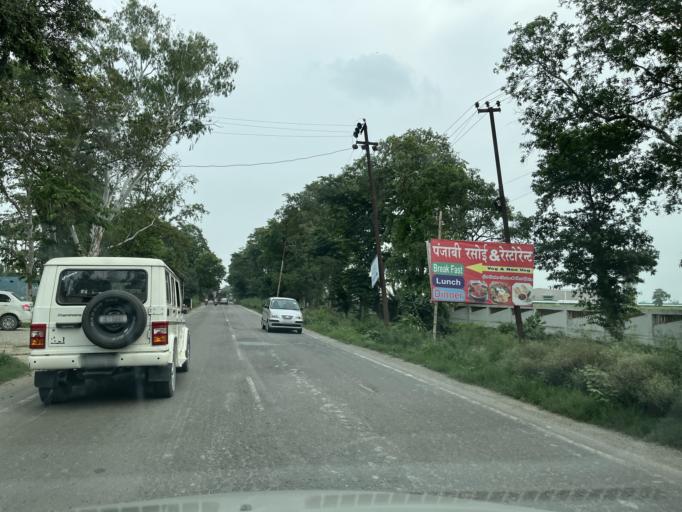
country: IN
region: Uttar Pradesh
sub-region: Rampur
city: Bilaspur
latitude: 29.0283
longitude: 79.2663
